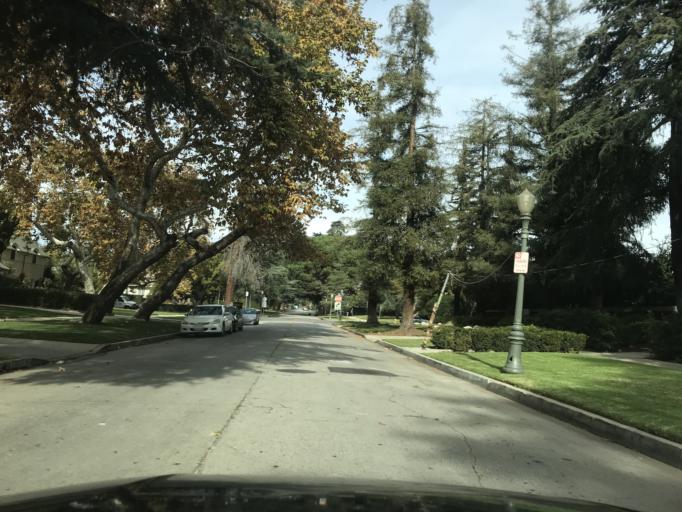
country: US
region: California
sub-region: Los Angeles County
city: Hollywood
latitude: 34.0628
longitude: -118.3200
